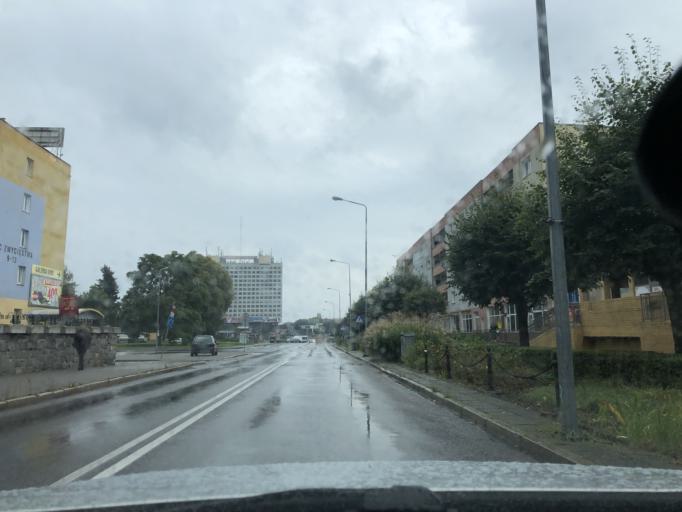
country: PL
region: Greater Poland Voivodeship
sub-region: Powiat pilski
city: Pila
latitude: 53.1505
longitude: 16.7334
